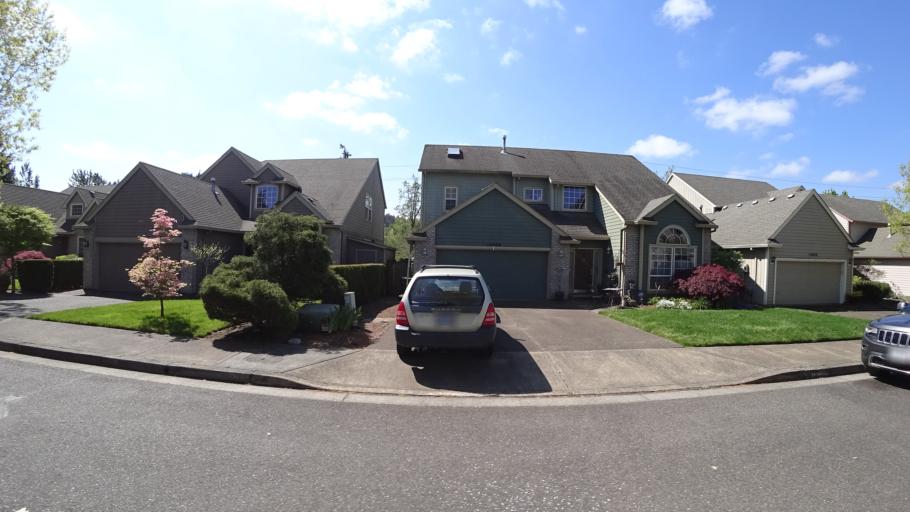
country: US
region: Oregon
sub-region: Washington County
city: King City
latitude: 45.4271
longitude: -122.8379
